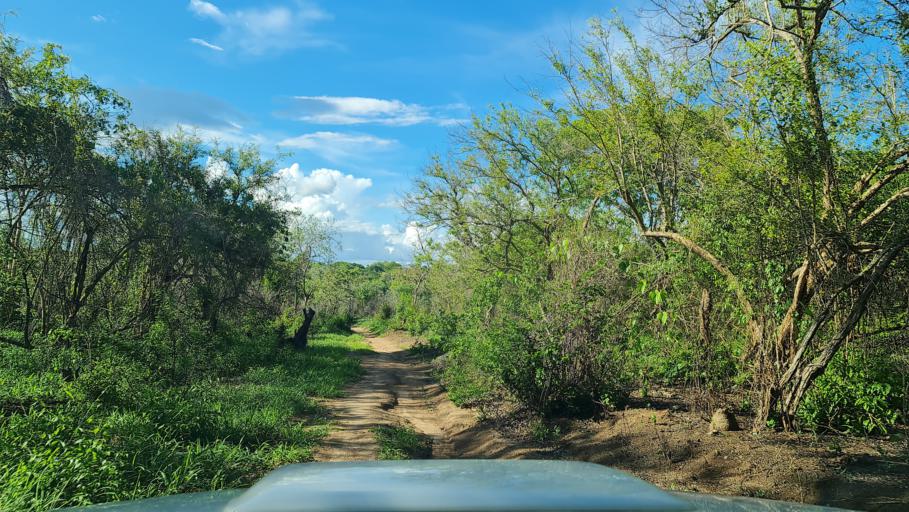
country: MZ
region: Nampula
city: Ilha de Mocambique
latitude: -15.2577
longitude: 40.1839
